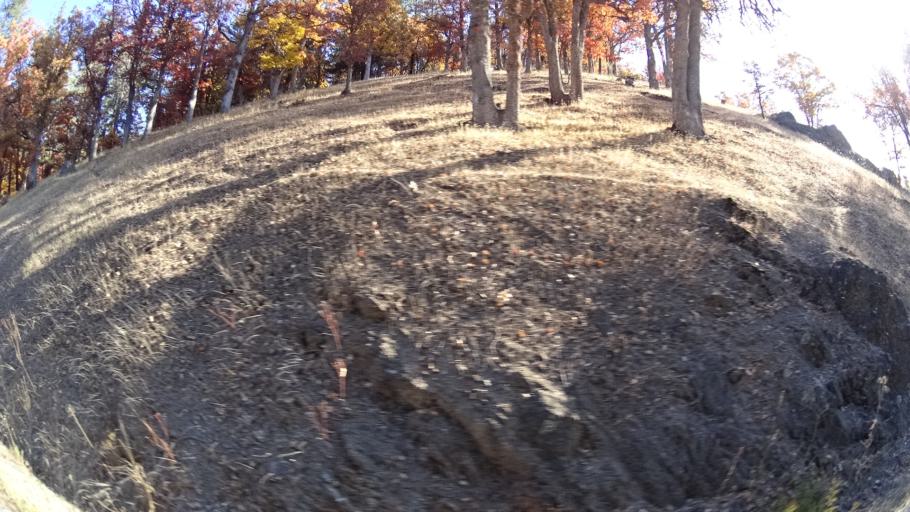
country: US
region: California
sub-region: Siskiyou County
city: Yreka
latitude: 41.6393
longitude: -122.9875
